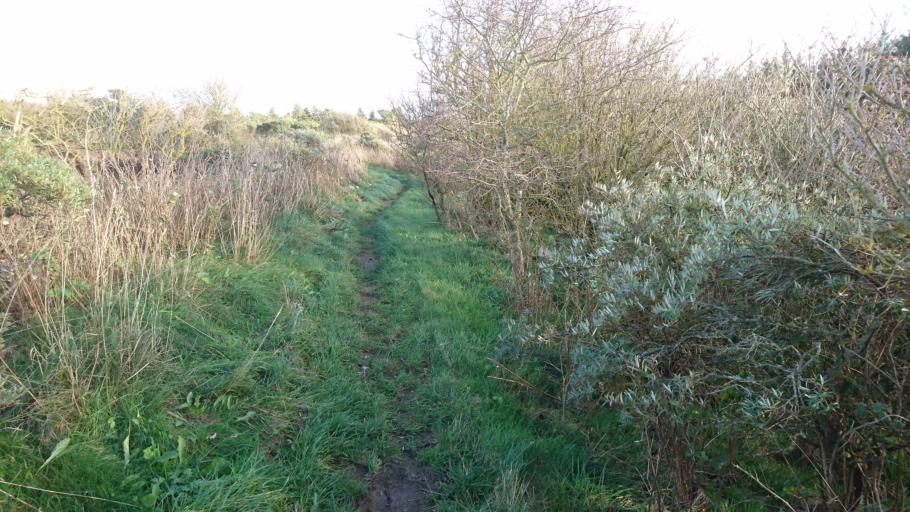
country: DK
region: North Denmark
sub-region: Morso Kommune
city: Nykobing Mors
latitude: 56.8373
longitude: 8.9592
